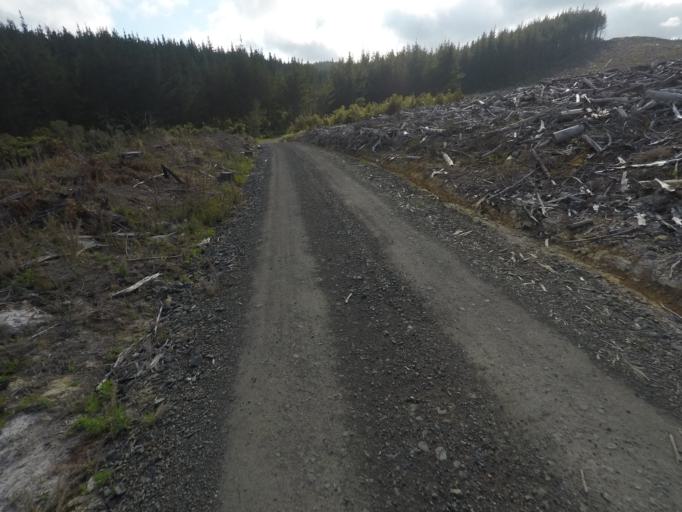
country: NZ
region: Auckland
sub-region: Auckland
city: Parakai
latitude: -36.7124
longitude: 174.5714
